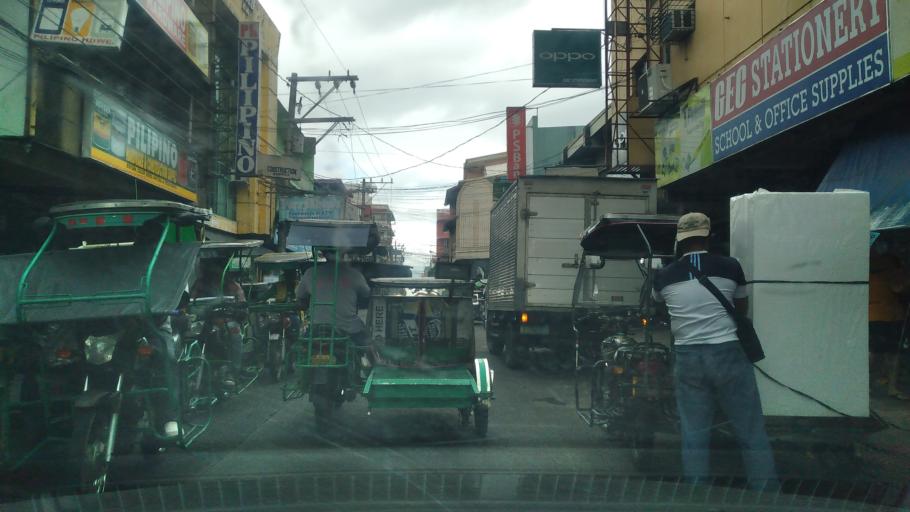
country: PH
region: Calabarzon
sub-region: Province of Quezon
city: Lucena
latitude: 13.9353
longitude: 121.6136
